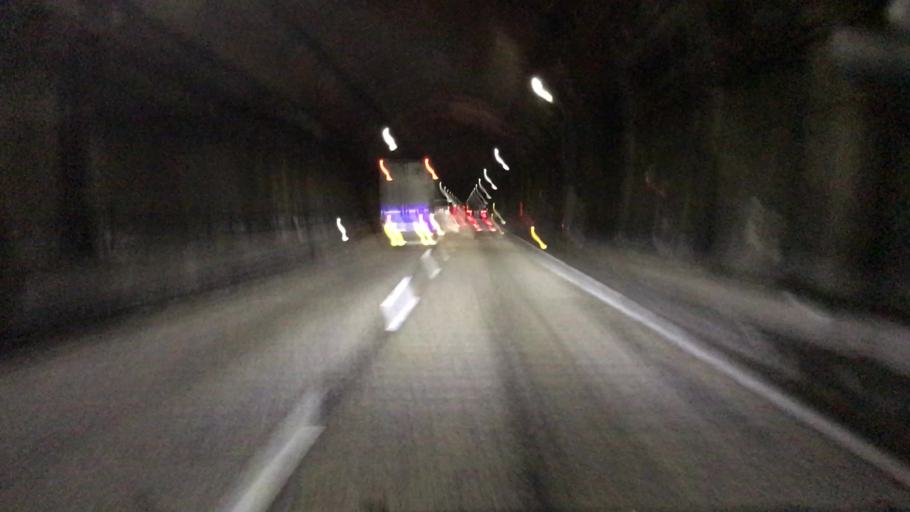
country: JP
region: Hyogo
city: Kobe
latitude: 34.7266
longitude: 135.1821
